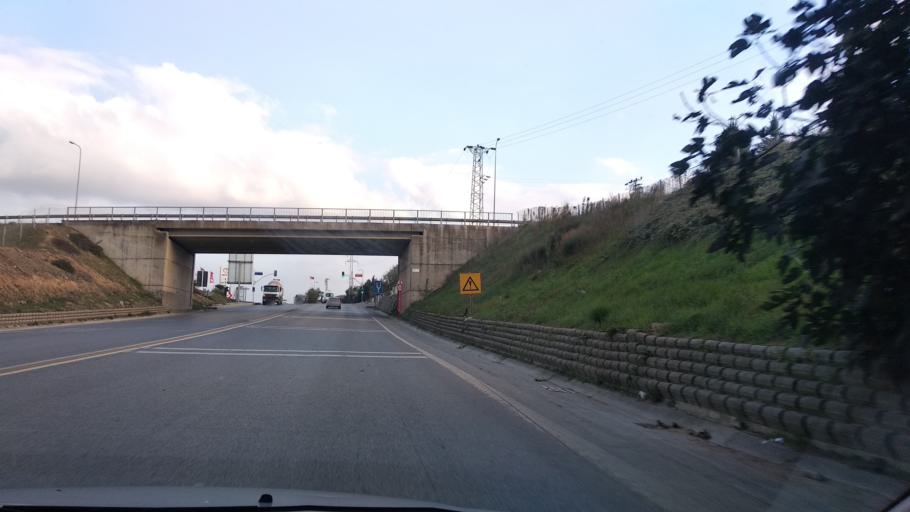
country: TR
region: Istanbul
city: Sultanbeyli
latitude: 40.9281
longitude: 29.3451
